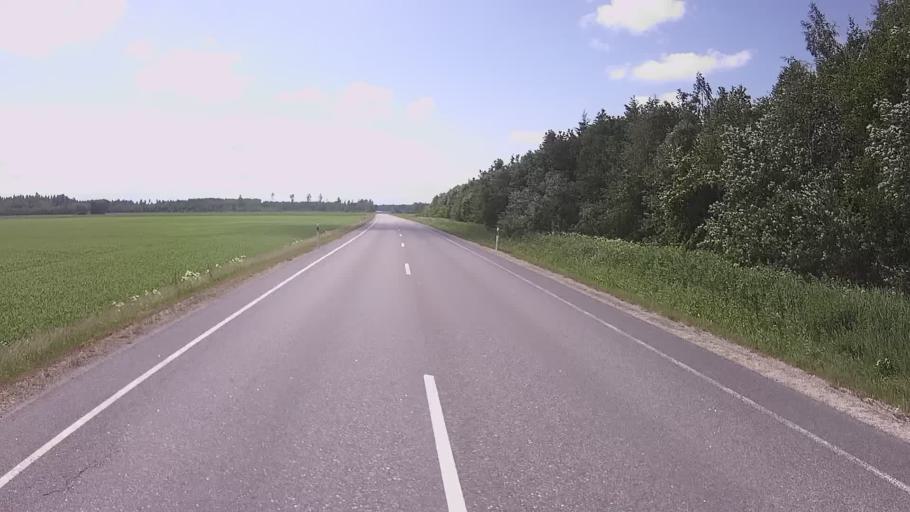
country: EE
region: Tartu
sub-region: Tartu linn
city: Tartu
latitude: 58.3910
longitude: 26.8915
